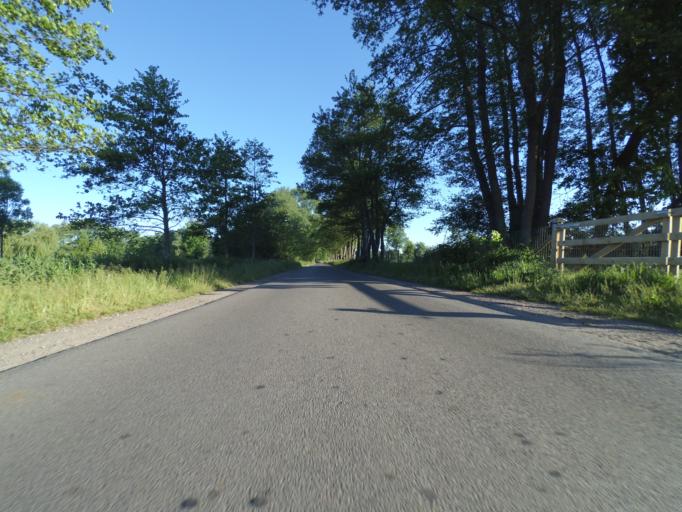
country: NL
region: Gelderland
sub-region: Gemeente Barneveld
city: Kootwijkerbroek
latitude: 52.1441
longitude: 5.7003
